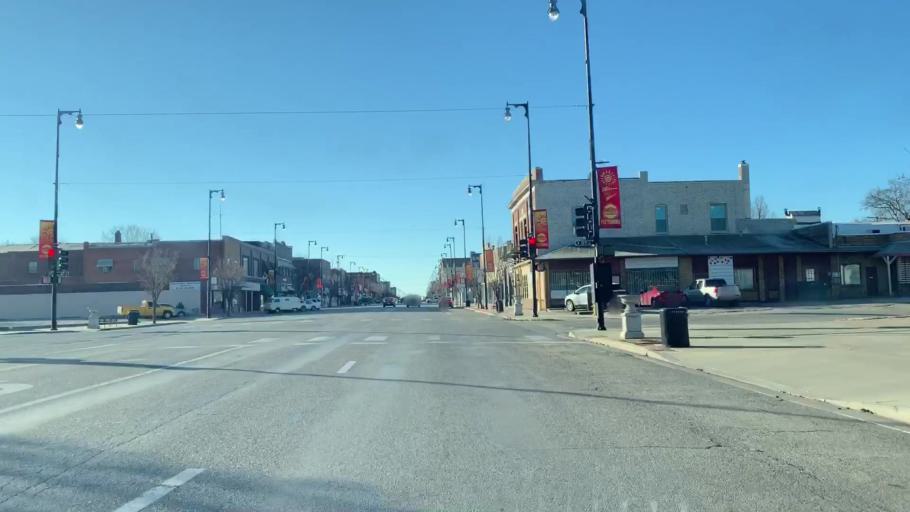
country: US
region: Kansas
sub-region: Crawford County
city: Pittsburg
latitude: 37.4173
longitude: -94.7050
